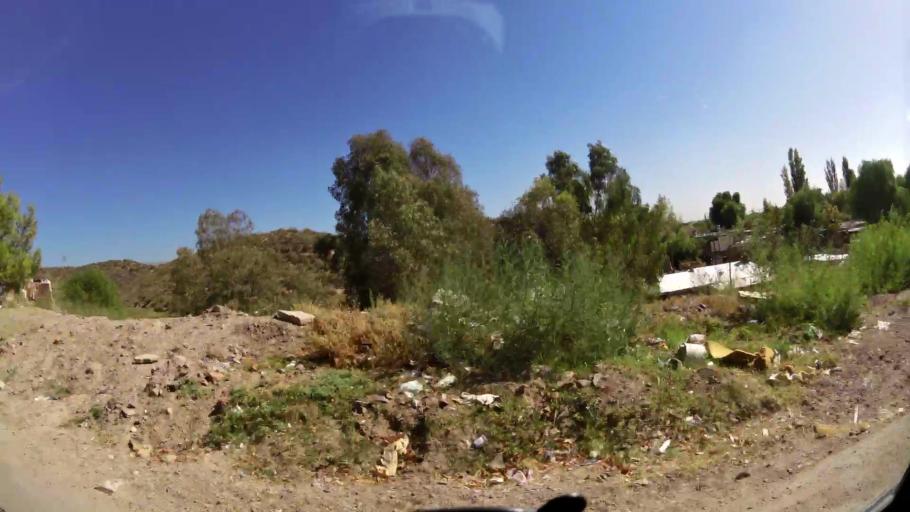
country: AR
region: Mendoza
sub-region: Departamento de Godoy Cruz
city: Godoy Cruz
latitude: -32.9093
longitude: -68.8828
